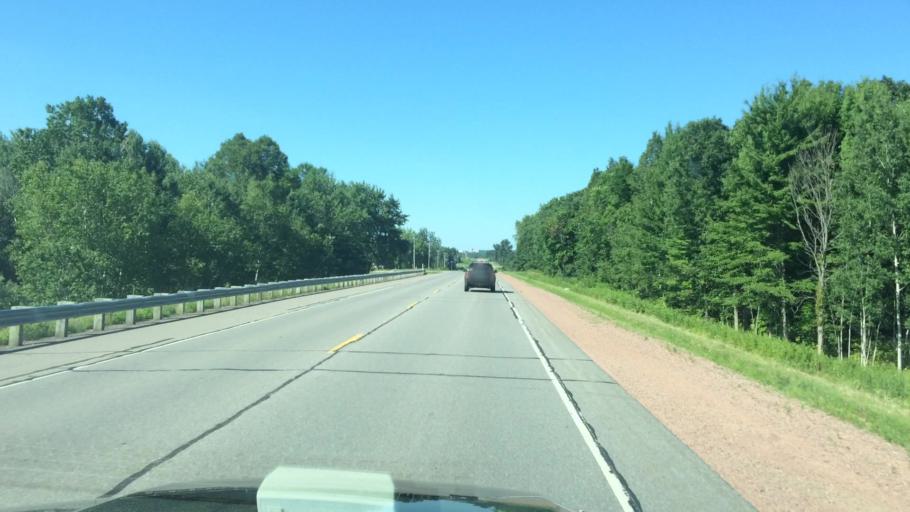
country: US
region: Wisconsin
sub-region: Wood County
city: Marshfield
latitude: 44.7155
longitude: -90.1113
